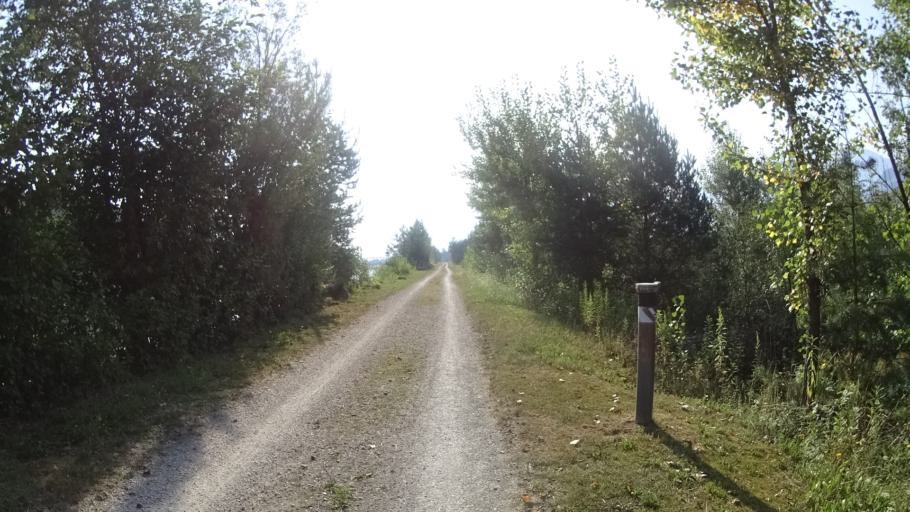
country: AT
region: Carinthia
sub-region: Politischer Bezirk Klagenfurt Land
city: Kottmannsdorf
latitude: 46.5426
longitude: 14.2476
